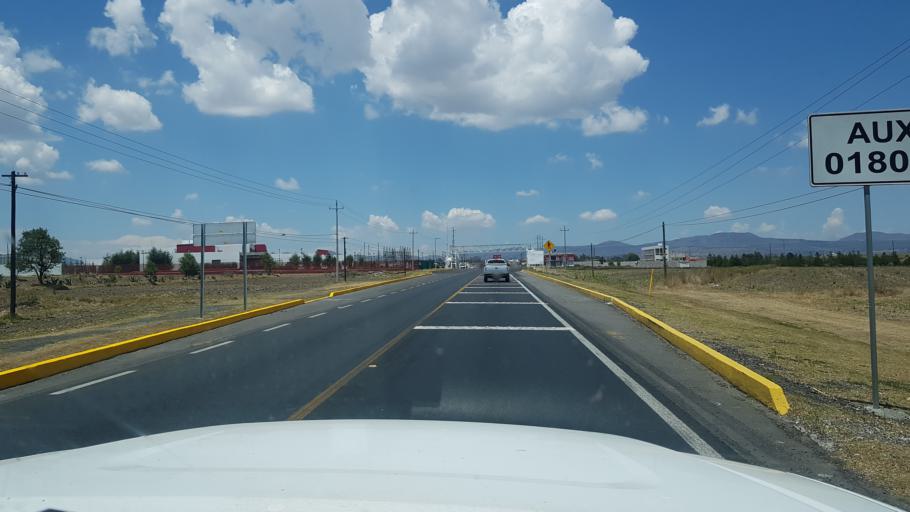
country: MX
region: Hidalgo
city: Calpulalpan
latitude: 19.5824
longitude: -98.5341
